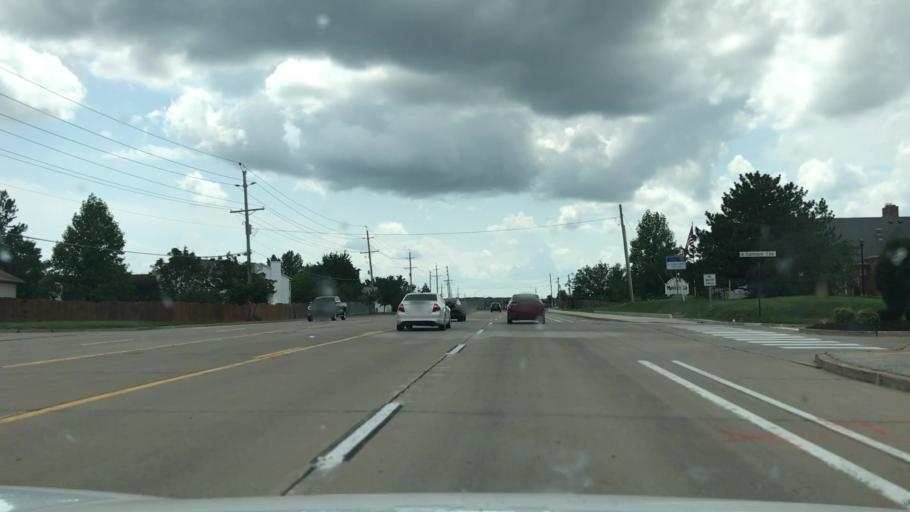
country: US
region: Missouri
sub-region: Saint Charles County
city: Weldon Spring
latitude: 38.7286
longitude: -90.6950
